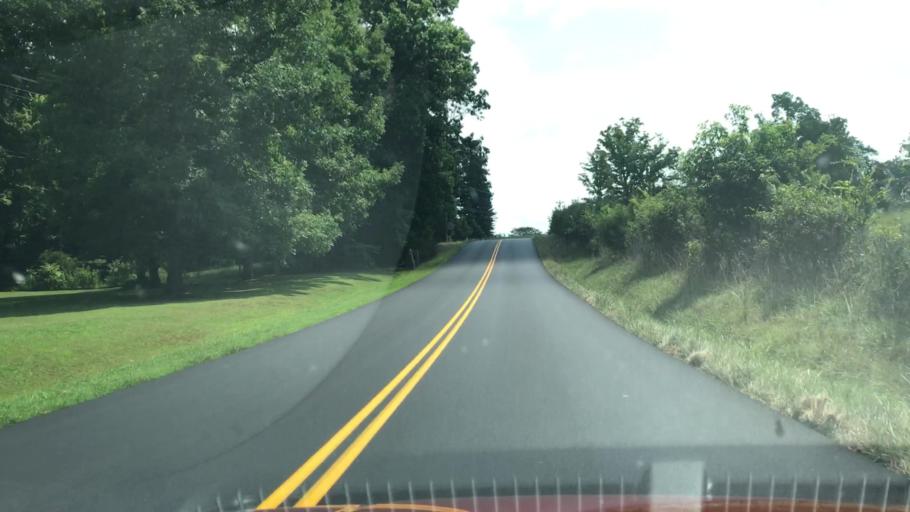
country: US
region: Kentucky
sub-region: Monroe County
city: Tompkinsville
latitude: 36.7364
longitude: -85.7485
